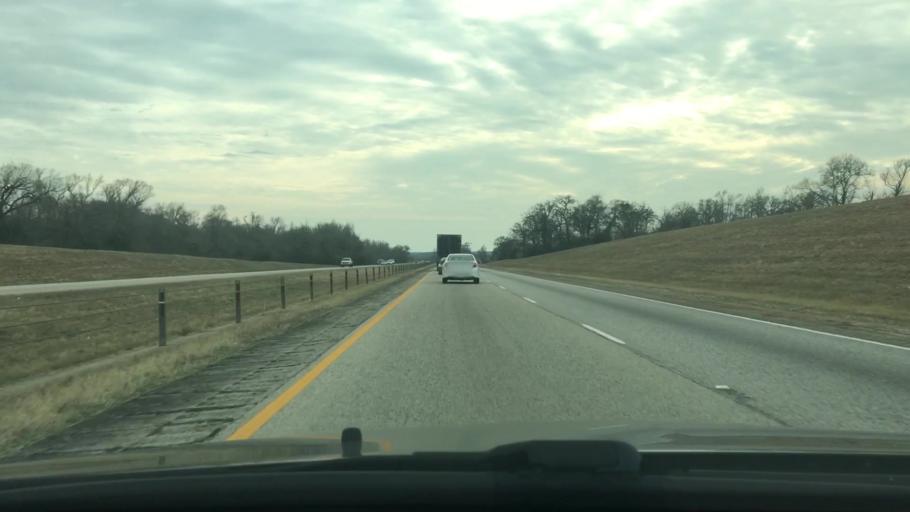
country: US
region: Texas
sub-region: Leon County
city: Centerville
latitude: 31.2216
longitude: -95.9958
